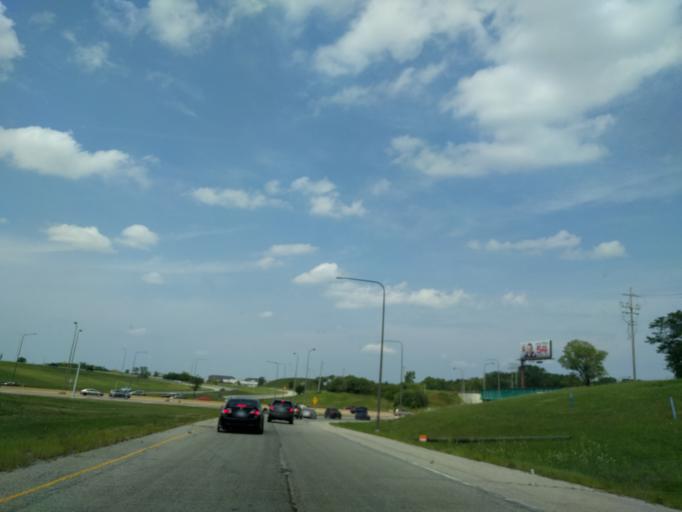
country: US
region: Illinois
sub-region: Cook County
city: Rosemont
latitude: 41.9805
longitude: -87.8766
